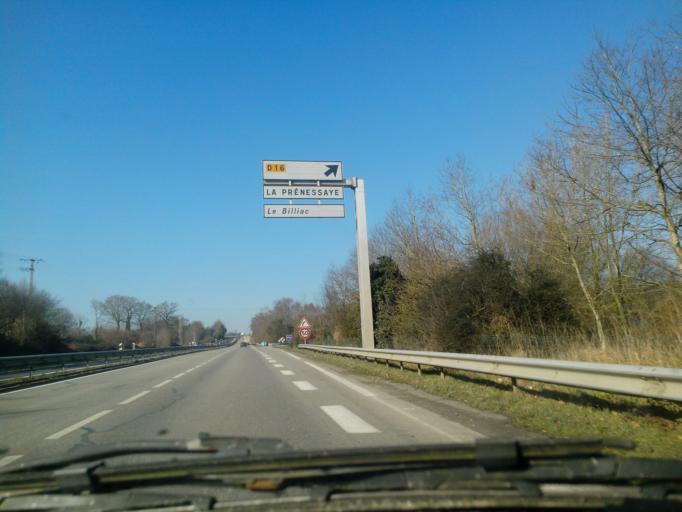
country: FR
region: Brittany
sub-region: Departement des Cotes-d'Armor
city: Plemet
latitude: 48.1740
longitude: -2.6548
